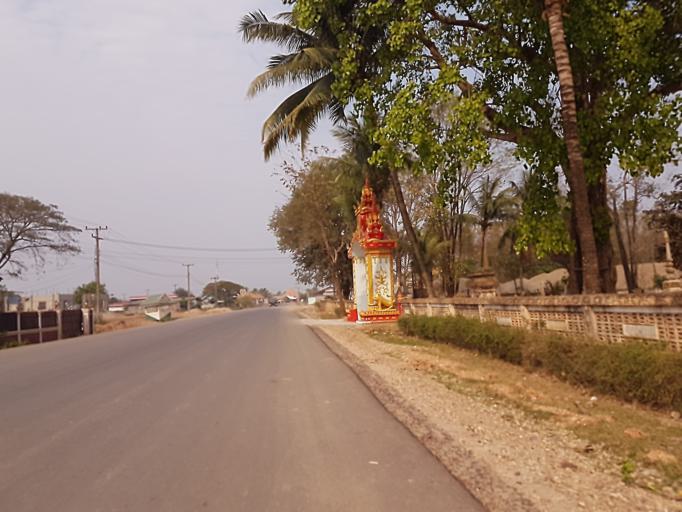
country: TH
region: Nong Khai
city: Nong Khai
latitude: 17.9638
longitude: 102.8372
